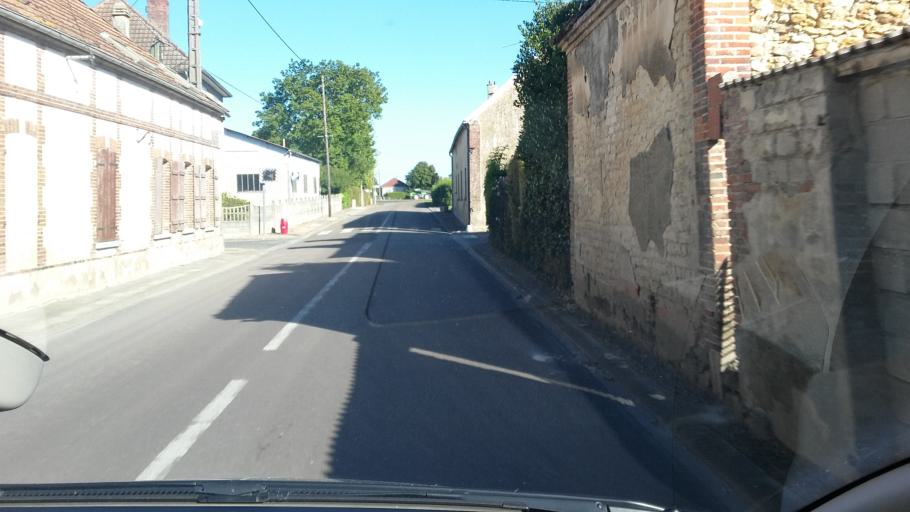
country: FR
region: Champagne-Ardenne
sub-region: Departement de la Marne
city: Connantre
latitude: 48.7883
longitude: 3.8811
